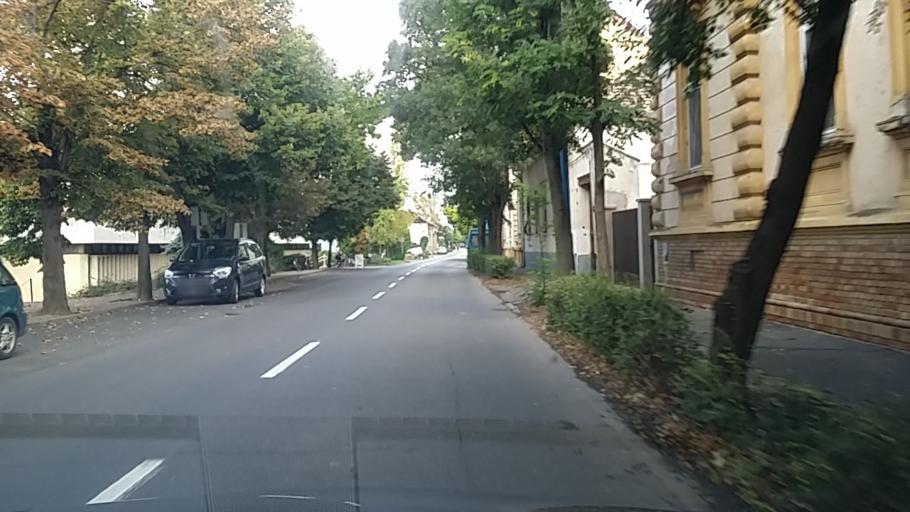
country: HU
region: Csongrad
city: Szentes
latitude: 46.6537
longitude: 20.2549
